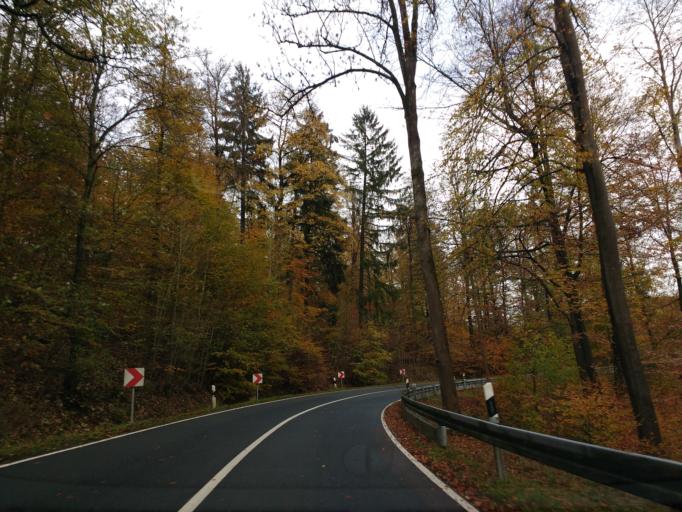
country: DE
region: Hesse
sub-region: Regierungsbezirk Kassel
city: Vohl
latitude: 51.1969
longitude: 8.9058
